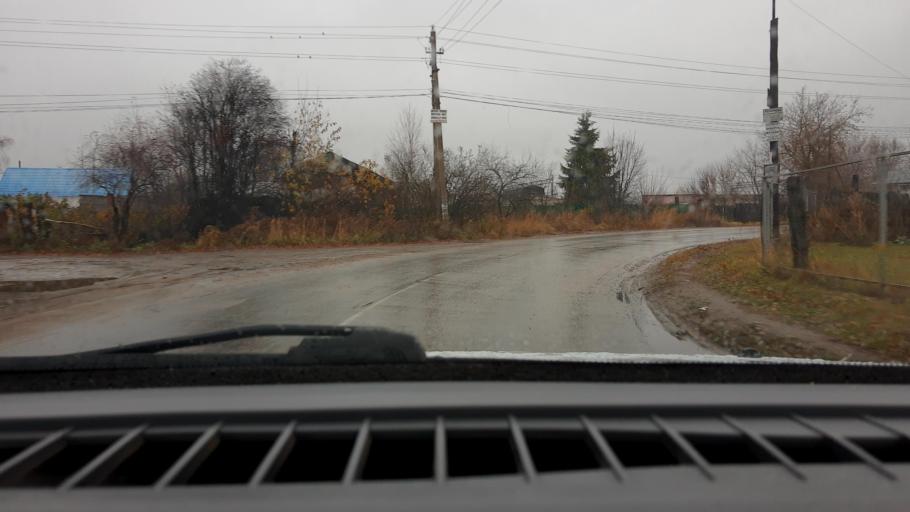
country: RU
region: Nizjnij Novgorod
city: Linda
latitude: 56.6817
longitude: 44.1962
